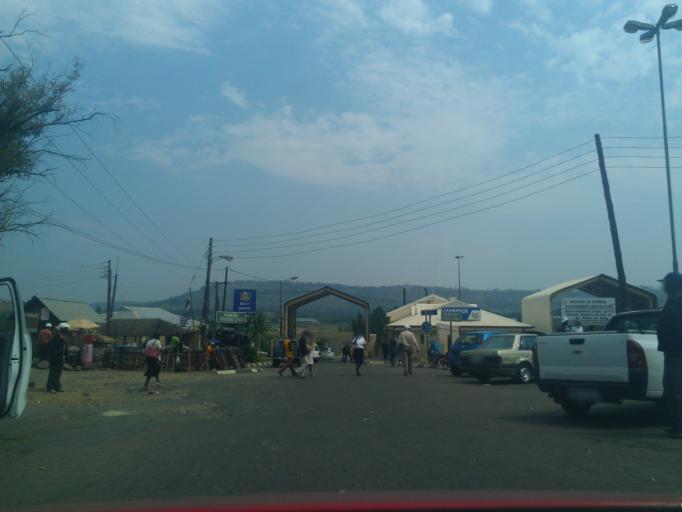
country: LS
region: Leribe
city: Maputsoe
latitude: -28.8859
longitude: 27.8931
